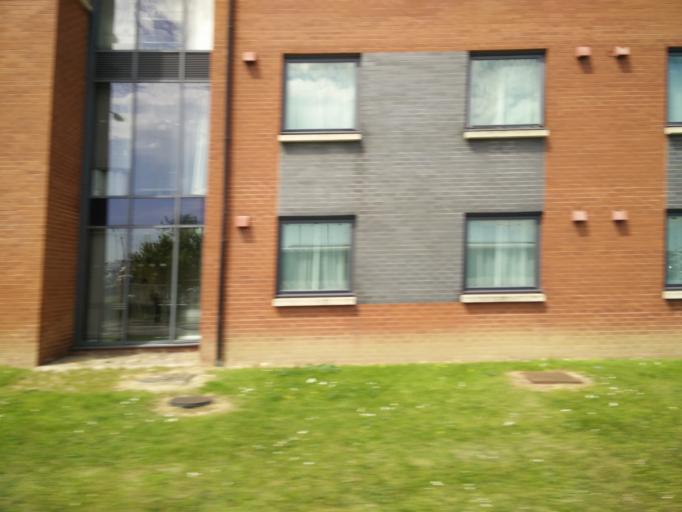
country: GB
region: England
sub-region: Luton
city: Luton
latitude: 51.8766
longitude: -0.3799
